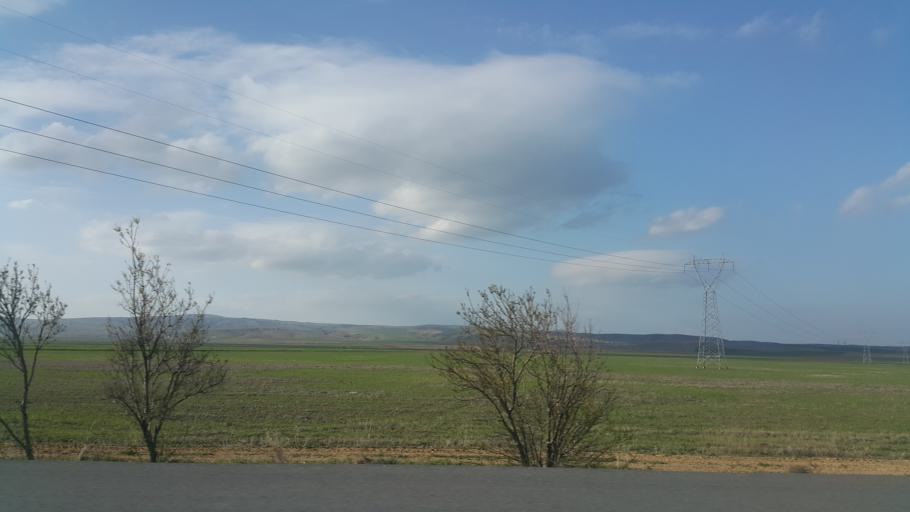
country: TR
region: Konya
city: Kulu
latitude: 39.1510
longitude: 33.2782
